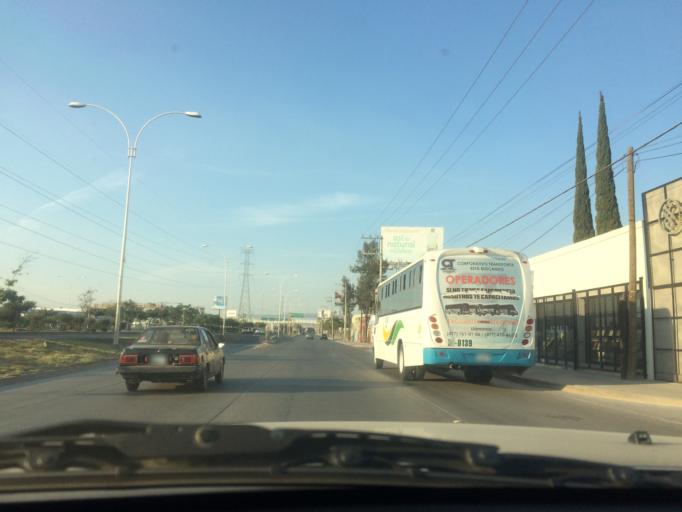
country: MX
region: Guanajuato
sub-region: Leon
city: Medina
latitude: 21.1070
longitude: -101.6234
